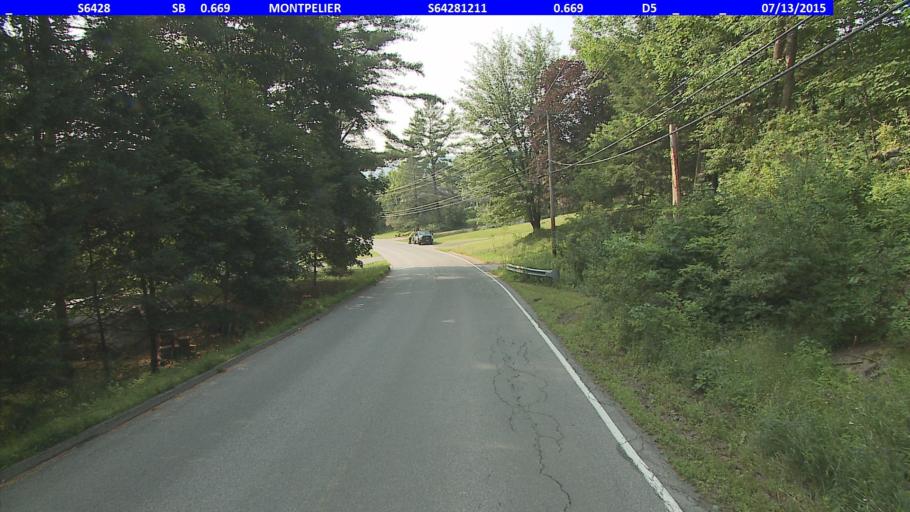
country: US
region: Vermont
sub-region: Washington County
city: Montpelier
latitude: 44.2716
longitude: -72.5910
